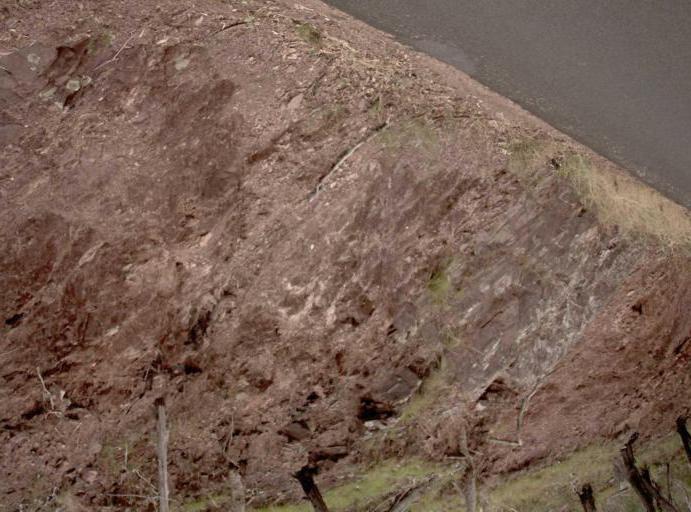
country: AU
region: Victoria
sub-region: Wellington
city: Heyfield
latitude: -37.7053
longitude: 146.6657
